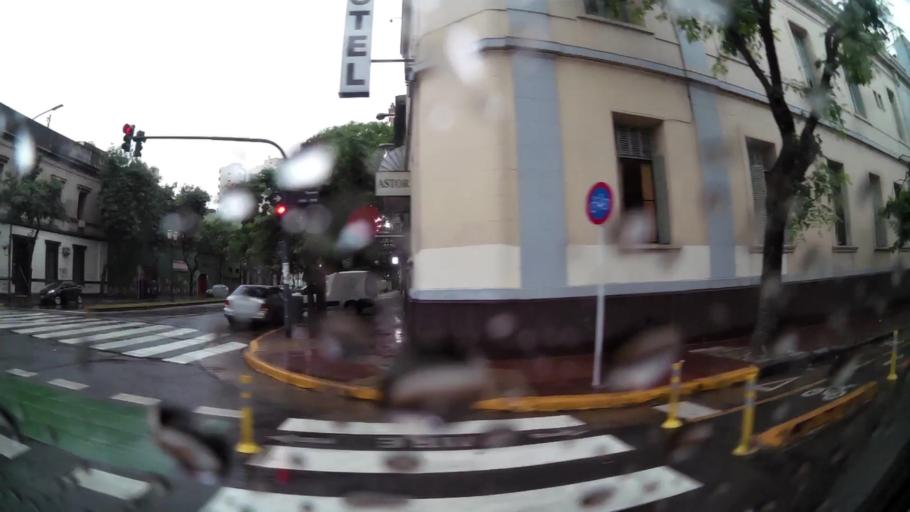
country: AR
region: Buenos Aires F.D.
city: Buenos Aires
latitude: -34.6280
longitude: -58.3765
